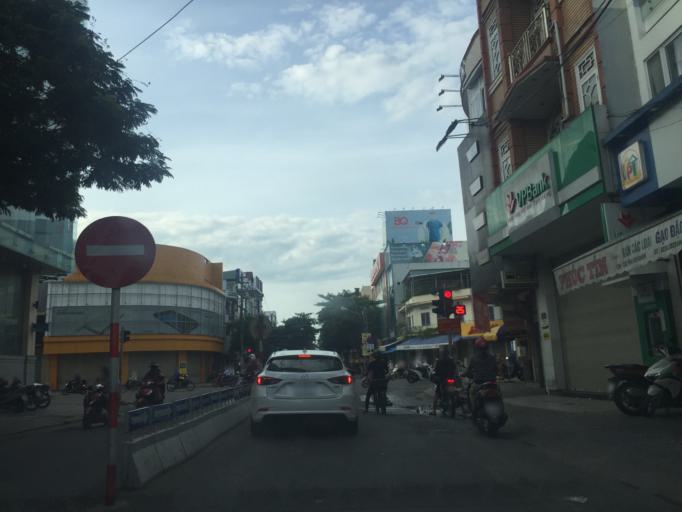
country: VN
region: Da Nang
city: Da Nang
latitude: 16.0706
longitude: 108.2134
